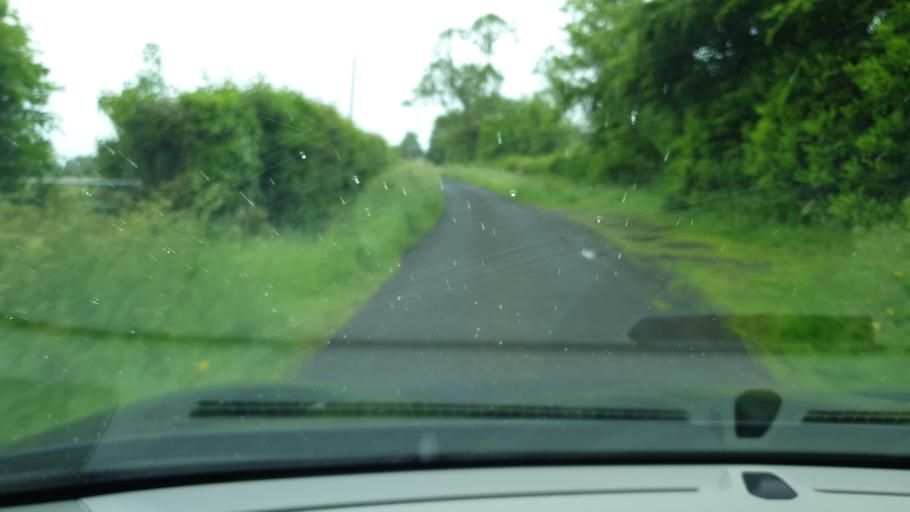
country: IE
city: Confey
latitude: 53.4324
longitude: -6.5300
